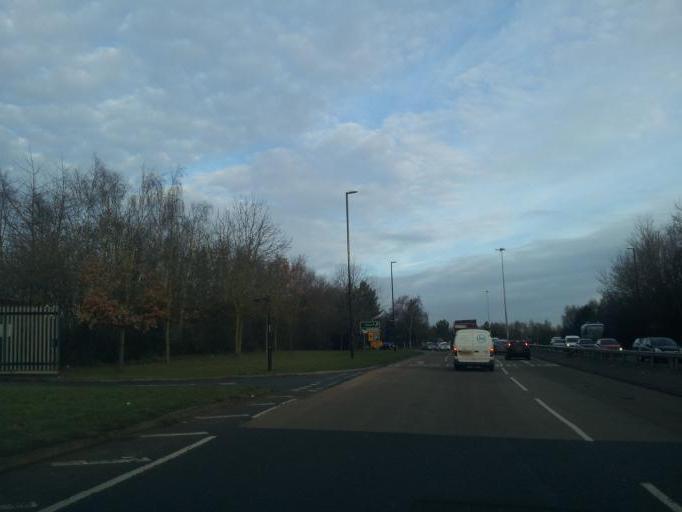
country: GB
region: England
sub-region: Warwickshire
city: Exhall
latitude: 52.4381
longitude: -1.4991
